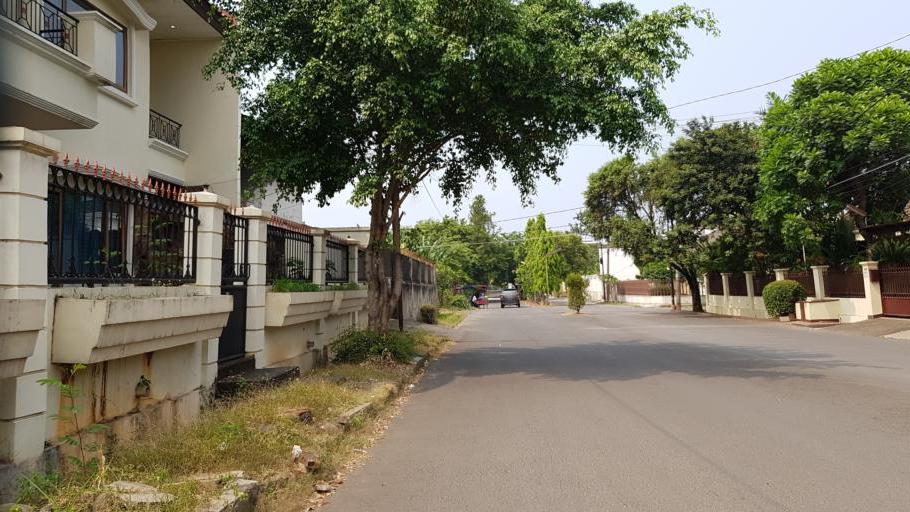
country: ID
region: West Java
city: Pamulang
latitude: -6.3283
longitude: 106.7870
